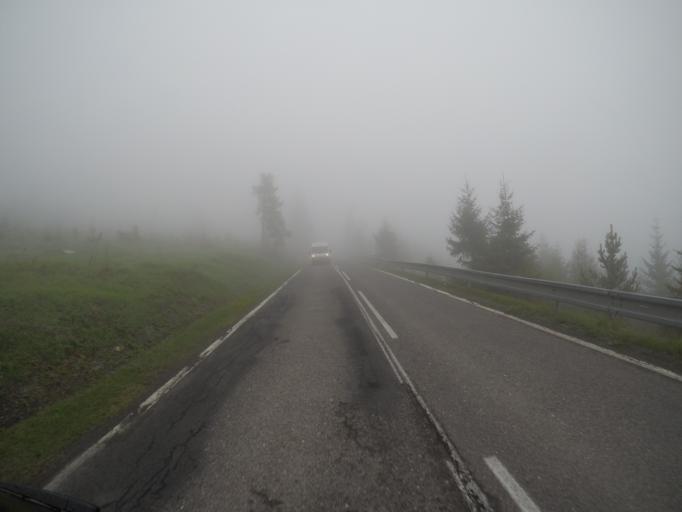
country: SK
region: Presovsky
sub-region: Okres Poprad
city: Strba
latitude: 49.1058
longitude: 20.0701
